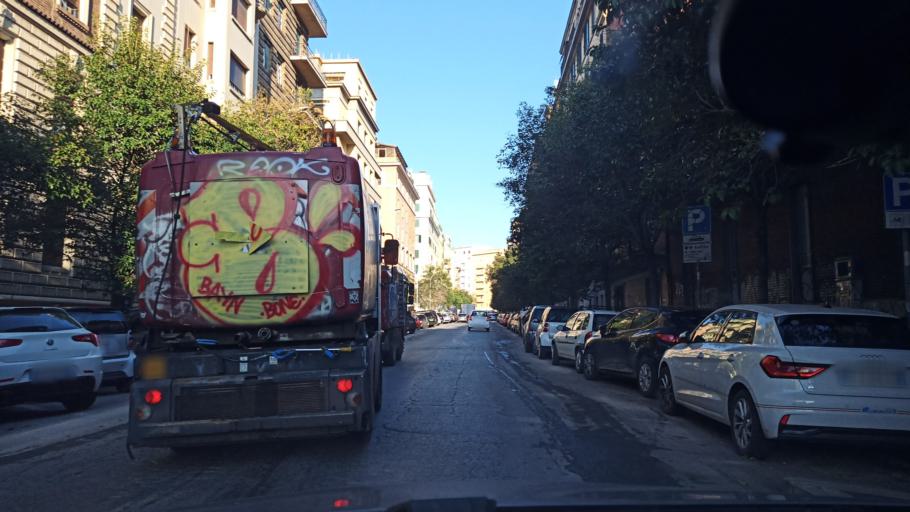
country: IT
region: Latium
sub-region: Citta metropolitana di Roma Capitale
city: Rome
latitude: 41.8800
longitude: 12.5133
